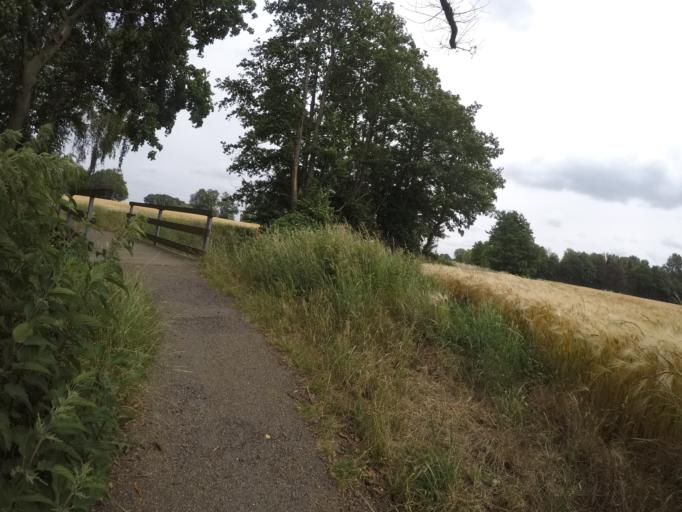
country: DE
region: North Rhine-Westphalia
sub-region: Regierungsbezirk Munster
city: Isselburg
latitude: 51.8531
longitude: 6.4382
